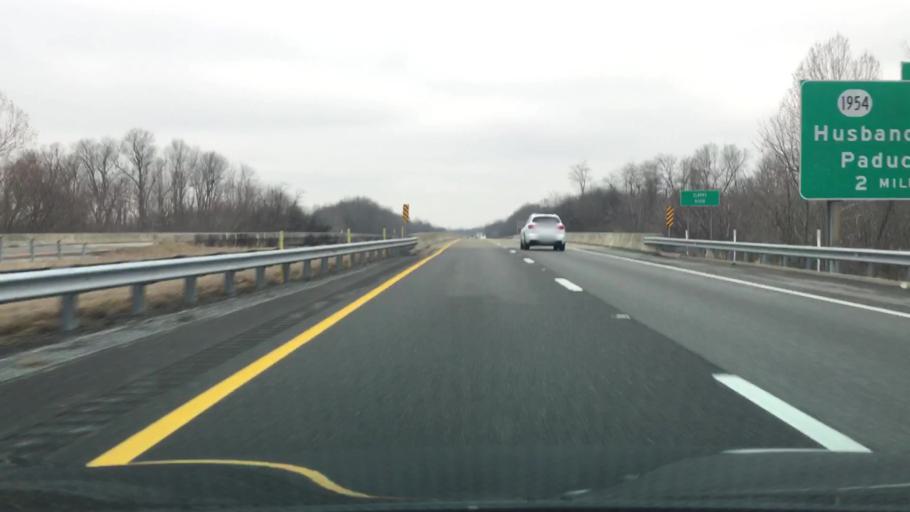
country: US
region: Kentucky
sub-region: McCracken County
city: Reidland
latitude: 37.0026
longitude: -88.5525
